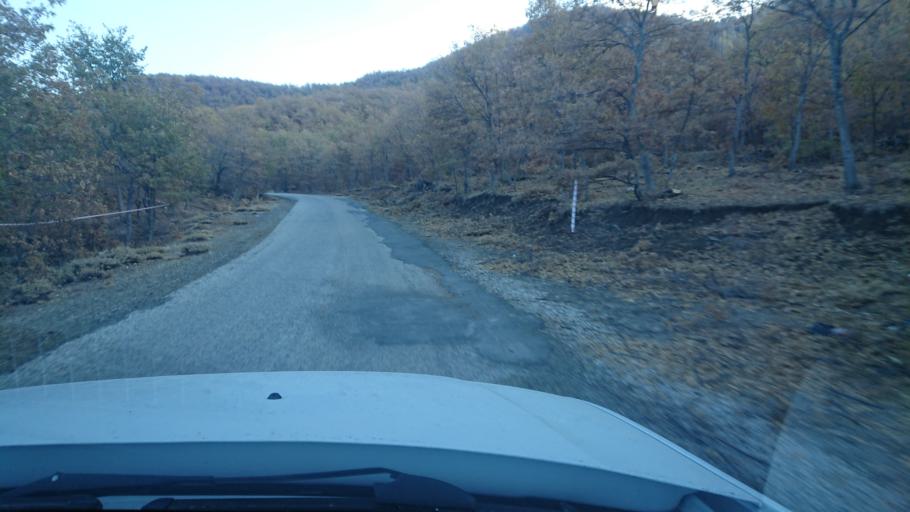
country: TR
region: Aksaray
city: Taspinar
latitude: 38.1670
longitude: 34.1943
